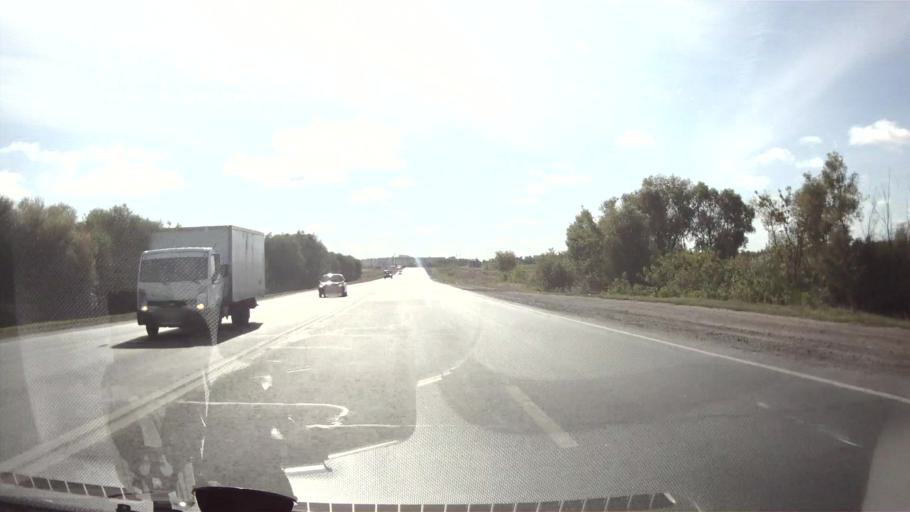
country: RU
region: Ulyanovsk
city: Isheyevka
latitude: 54.3024
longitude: 48.2433
